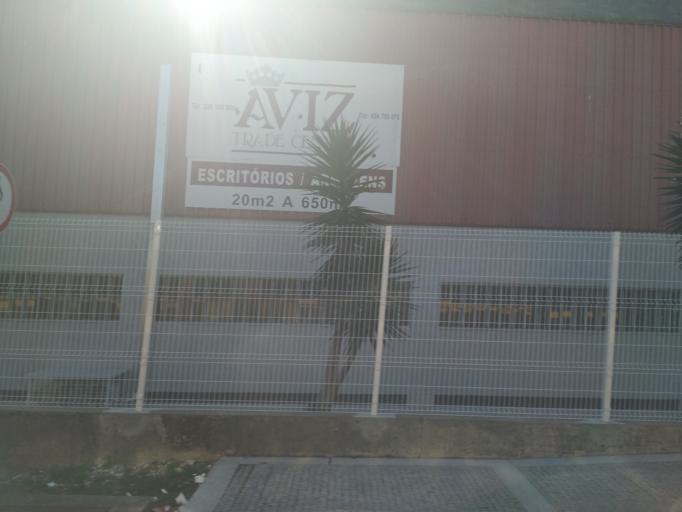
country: PT
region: Porto
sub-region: Matosinhos
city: Senhora da Hora
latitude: 41.1769
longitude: -8.6463
